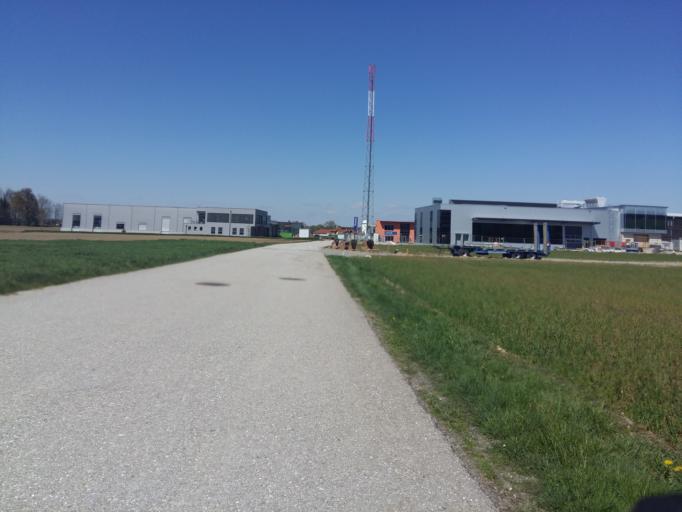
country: AT
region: Upper Austria
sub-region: Politischer Bezirk Scharding
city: Sankt Marienkirchen bei Schaerding
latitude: 48.3877
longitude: 13.4446
